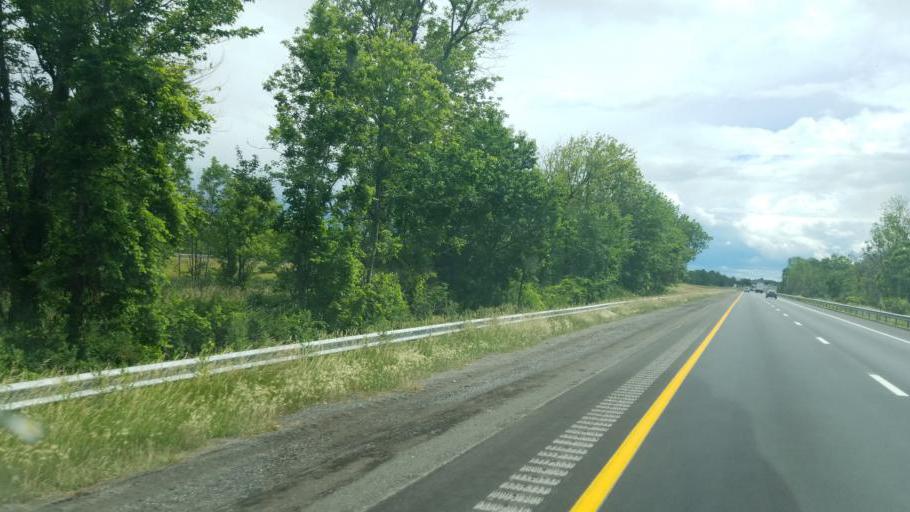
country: US
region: New York
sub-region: Genesee County
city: Bergen
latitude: 43.0290
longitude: -77.9251
